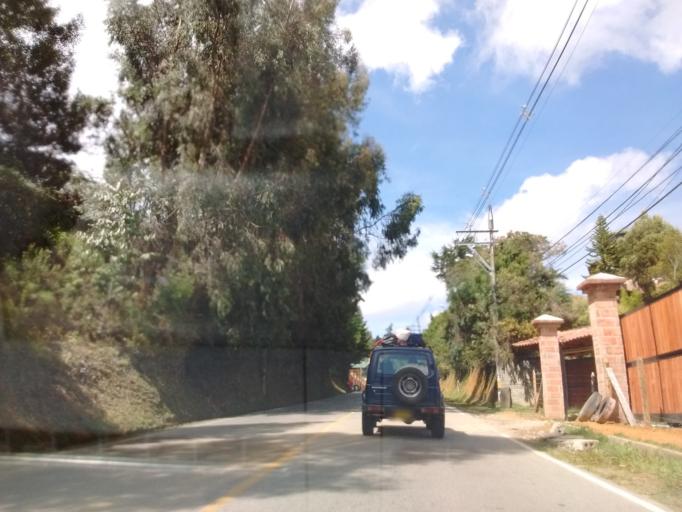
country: CO
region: Antioquia
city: Medellin
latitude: 6.2181
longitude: -75.5018
